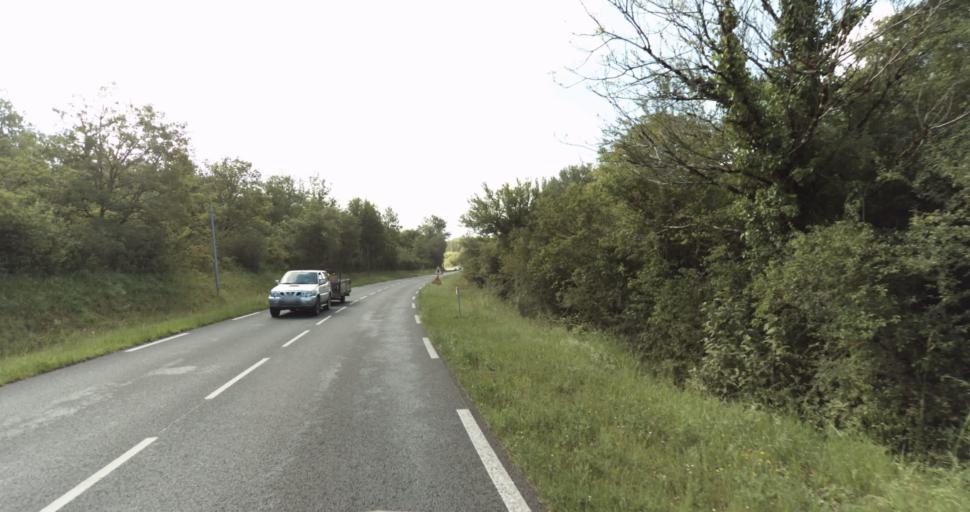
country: FR
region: Aquitaine
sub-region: Departement de la Dordogne
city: Le Bugue
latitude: 44.8444
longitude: 0.8494
